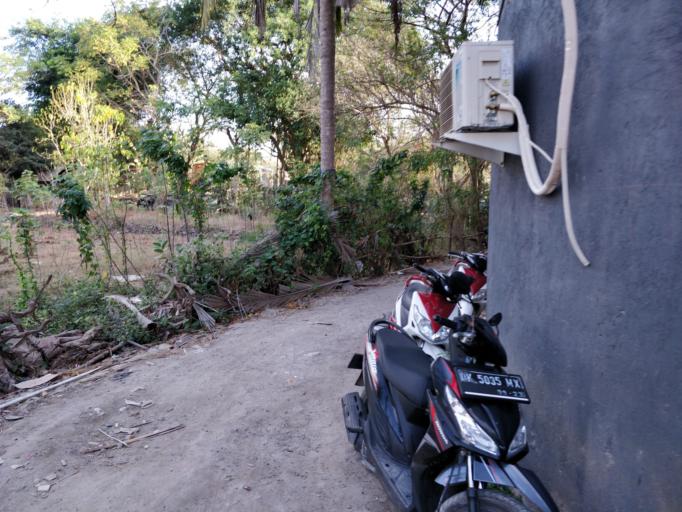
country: ID
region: Bali
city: Lembongan Kawan
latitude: -8.6836
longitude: 115.4325
